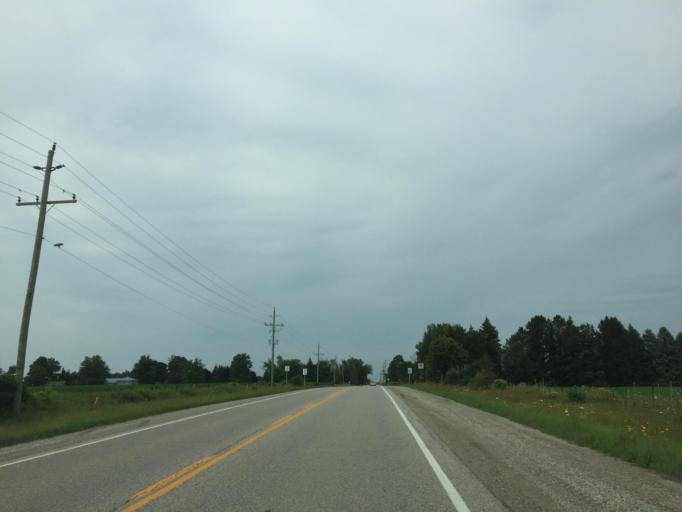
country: CA
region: Ontario
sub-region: Wellington County
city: Guelph
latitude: 43.5822
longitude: -80.3044
